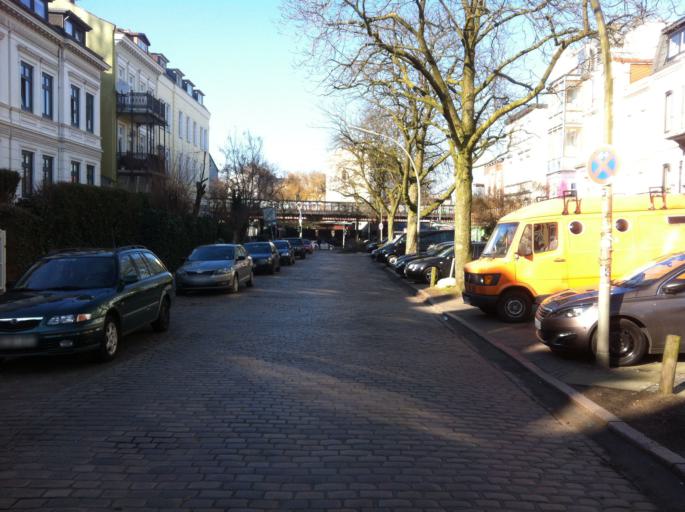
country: DE
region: Hamburg
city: St. Pauli
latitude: 53.5603
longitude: 9.9550
